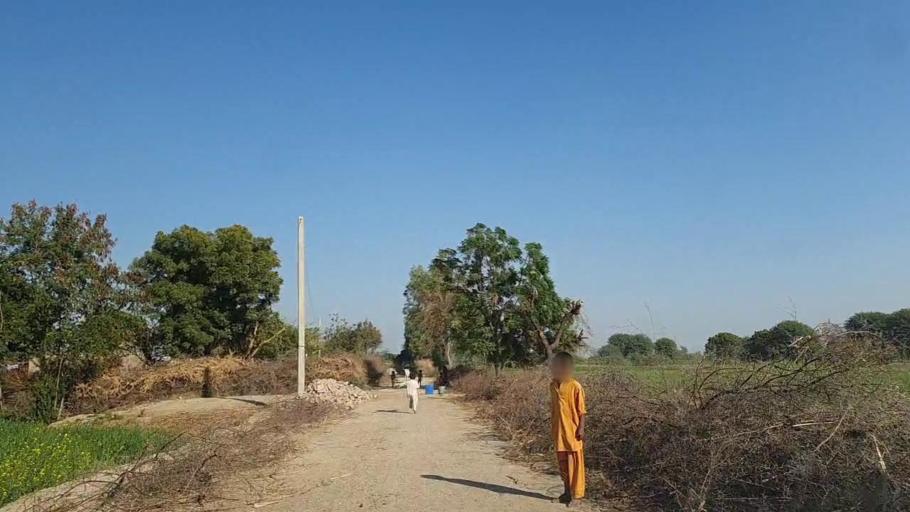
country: PK
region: Sindh
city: Samaro
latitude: 25.3615
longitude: 69.3947
